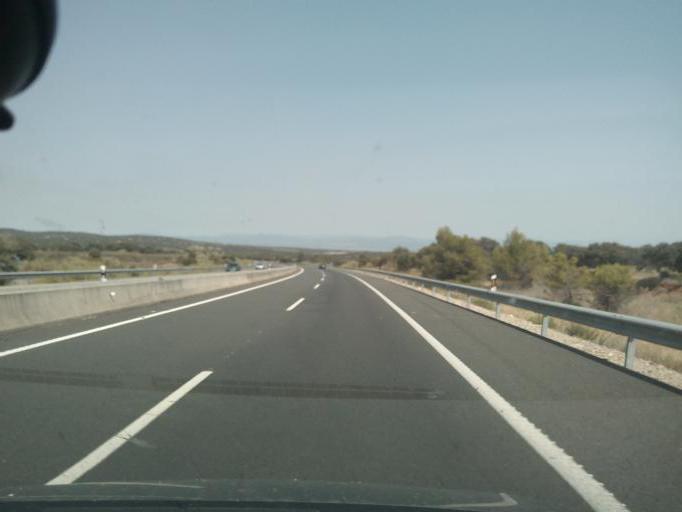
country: ES
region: Extremadura
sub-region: Provincia de Caceres
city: Casas de Miravete
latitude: 39.7640
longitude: -5.7338
